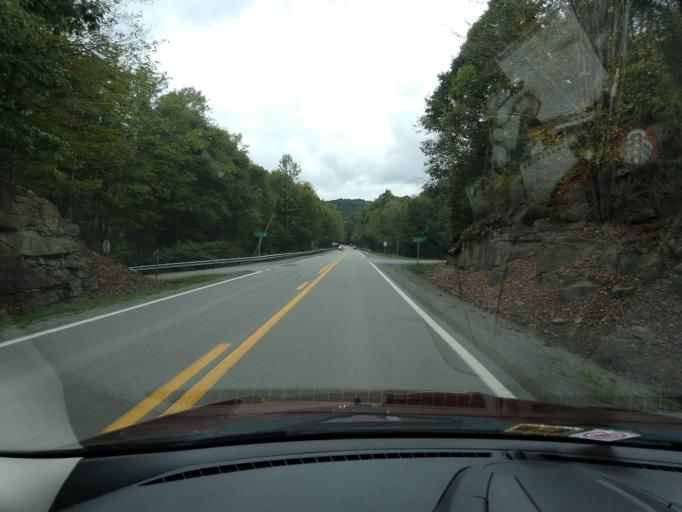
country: US
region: West Virginia
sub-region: Barbour County
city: Philippi
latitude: 39.1233
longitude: -79.9968
